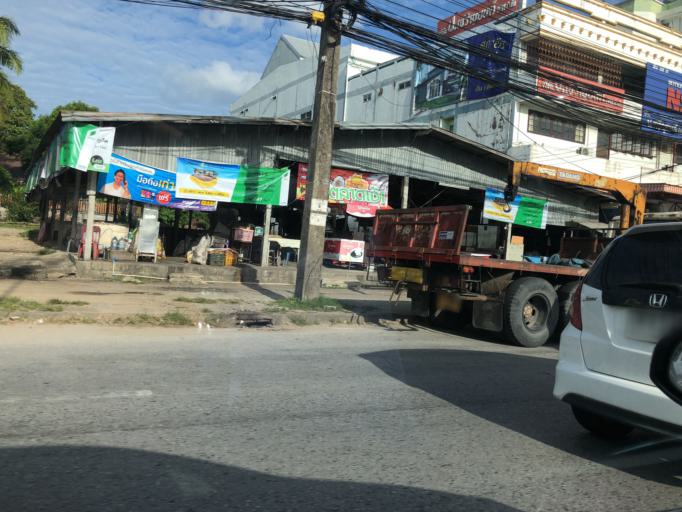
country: TH
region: Phuket
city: Ban Ratsada
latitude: 7.9158
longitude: 98.3938
